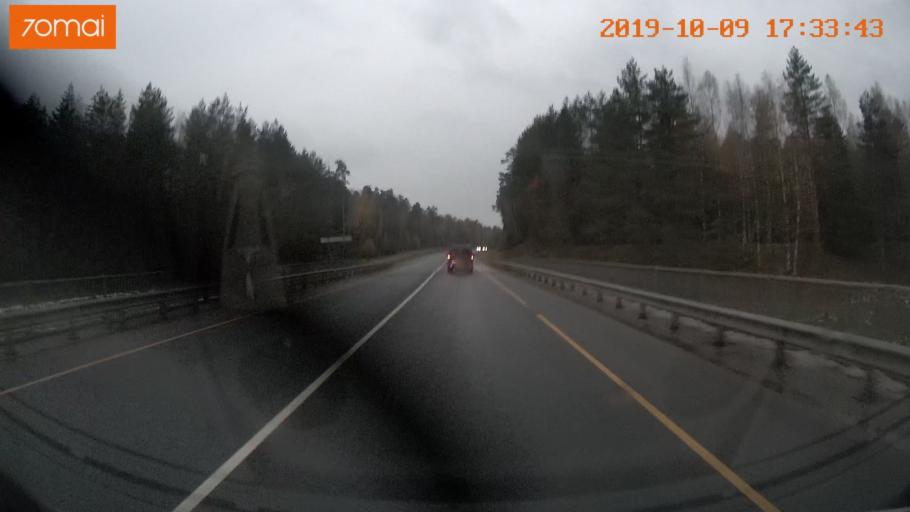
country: RU
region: Ivanovo
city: Bogorodskoye
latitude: 57.1144
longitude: 41.0180
